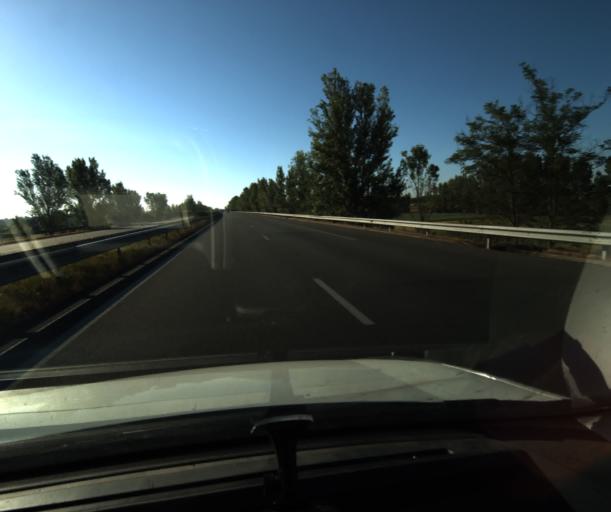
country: FR
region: Midi-Pyrenees
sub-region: Departement du Tarn-et-Garonne
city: Montech
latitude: 43.9853
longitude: 1.2440
